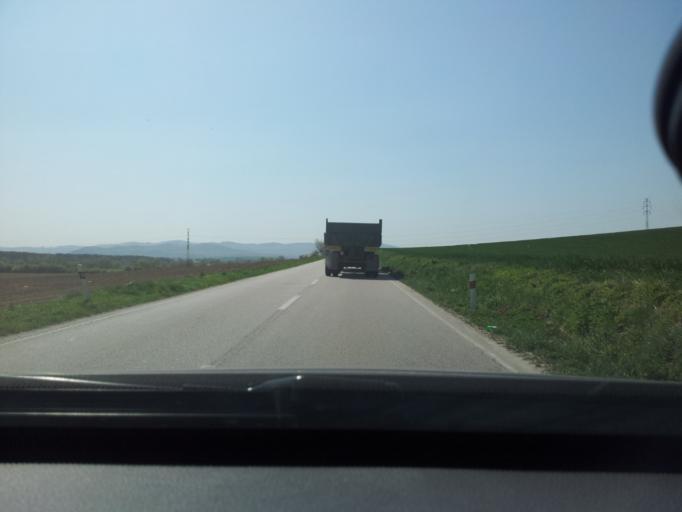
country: SK
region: Nitriansky
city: Banovce nad Bebravou
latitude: 48.6347
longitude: 18.2539
